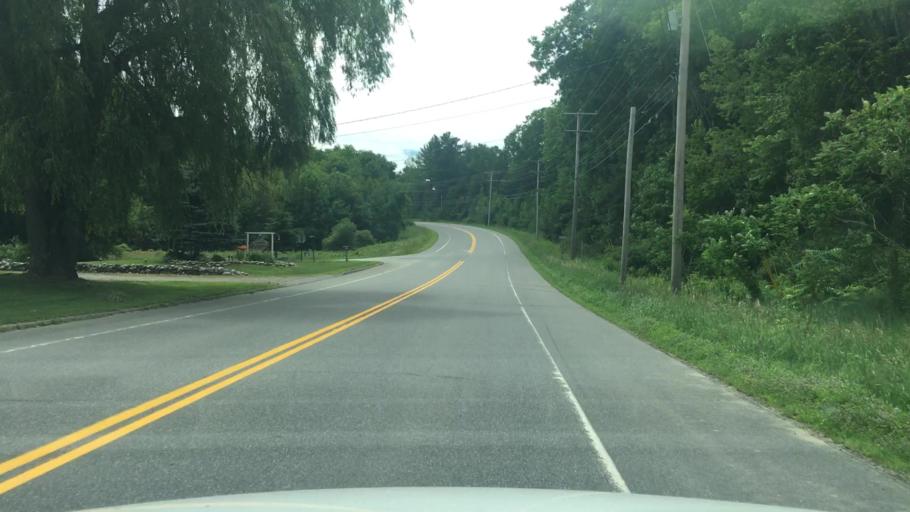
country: US
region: Maine
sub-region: Waldo County
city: Troy
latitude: 44.5698
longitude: -69.2796
